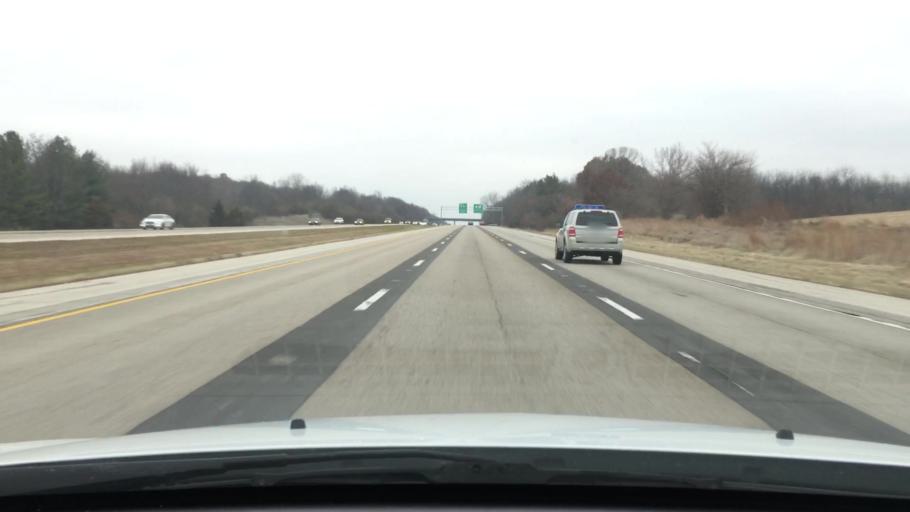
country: US
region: Illinois
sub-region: Logan County
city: Lincoln
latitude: 40.1392
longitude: -89.4170
